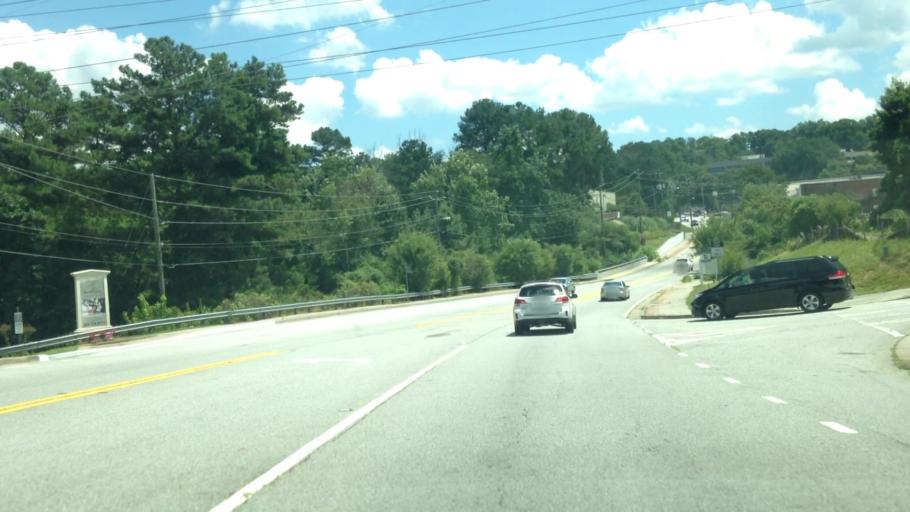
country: US
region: Georgia
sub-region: DeKalb County
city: North Atlanta
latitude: 33.8428
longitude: -84.3228
